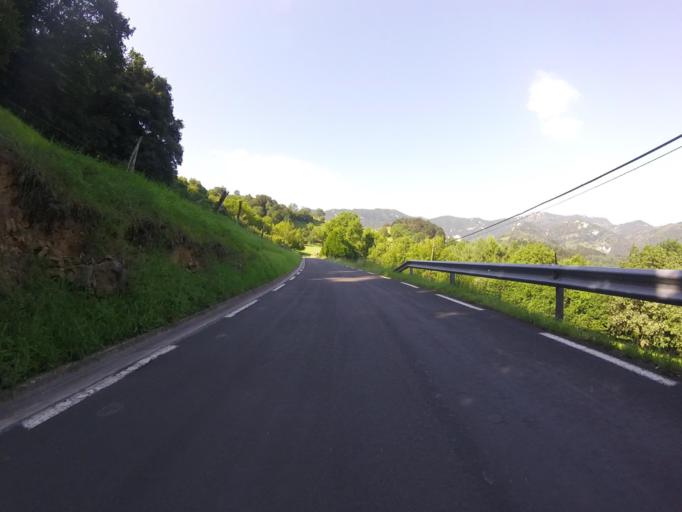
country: ES
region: Basque Country
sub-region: Provincia de Guipuzcoa
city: Alquiza
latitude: 43.1764
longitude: -2.0985
